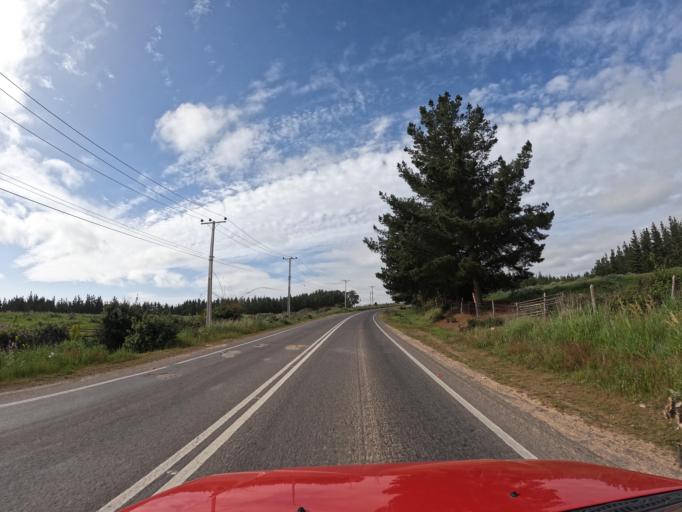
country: CL
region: O'Higgins
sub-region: Provincia de Colchagua
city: Santa Cruz
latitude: -34.3556
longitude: -71.9433
